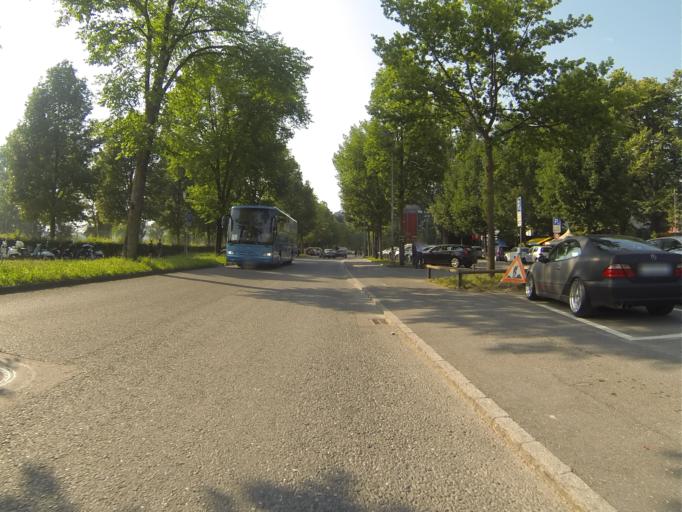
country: CH
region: Lucerne
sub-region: Lucerne-Land District
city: Adligenswil
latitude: 47.0509
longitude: 8.3365
